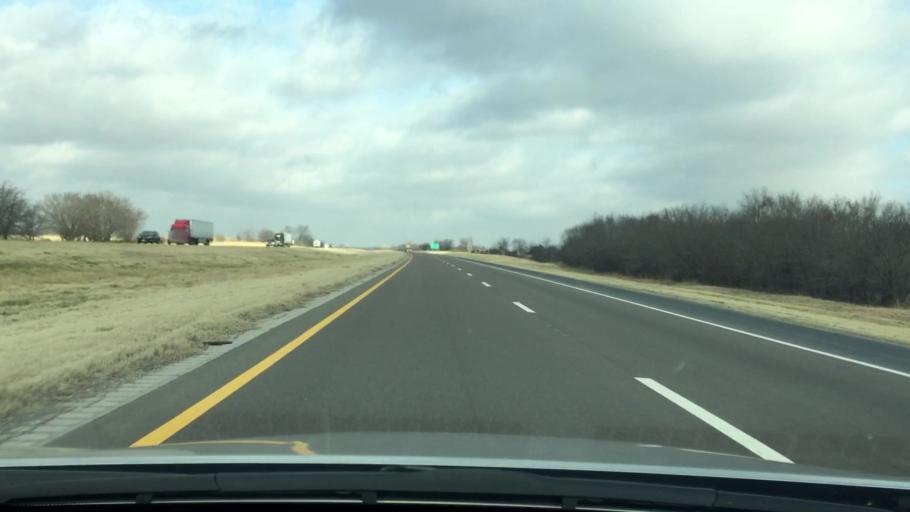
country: US
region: Oklahoma
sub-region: Garvin County
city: Maysville
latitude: 34.8346
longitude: -97.3123
